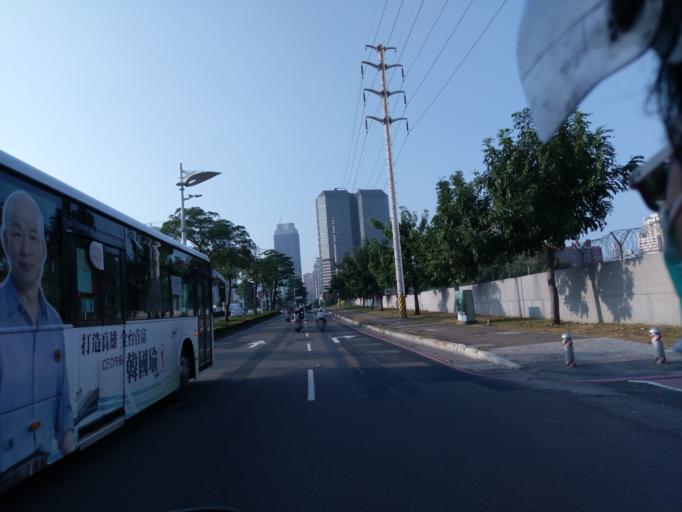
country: TW
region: Kaohsiung
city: Kaohsiung
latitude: 22.6008
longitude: 120.3125
